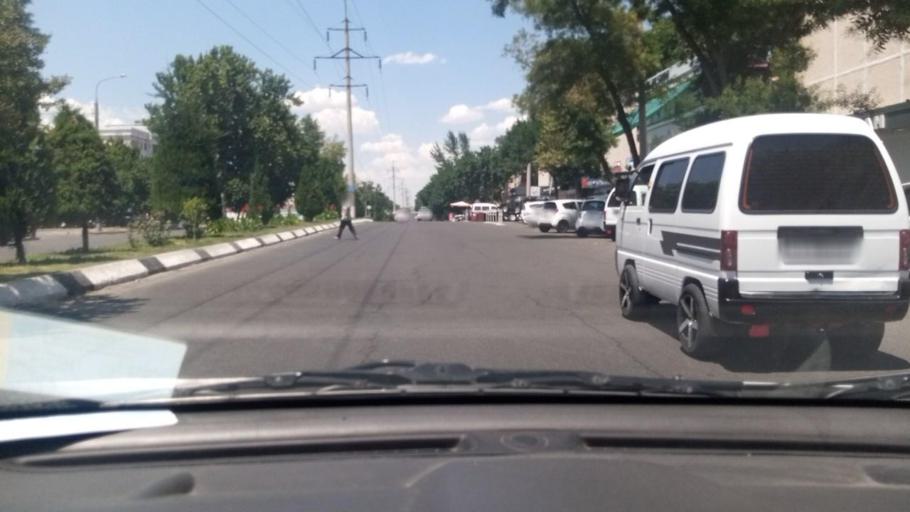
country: UZ
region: Toshkent Shahri
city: Tashkent
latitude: 41.2840
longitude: 69.1947
